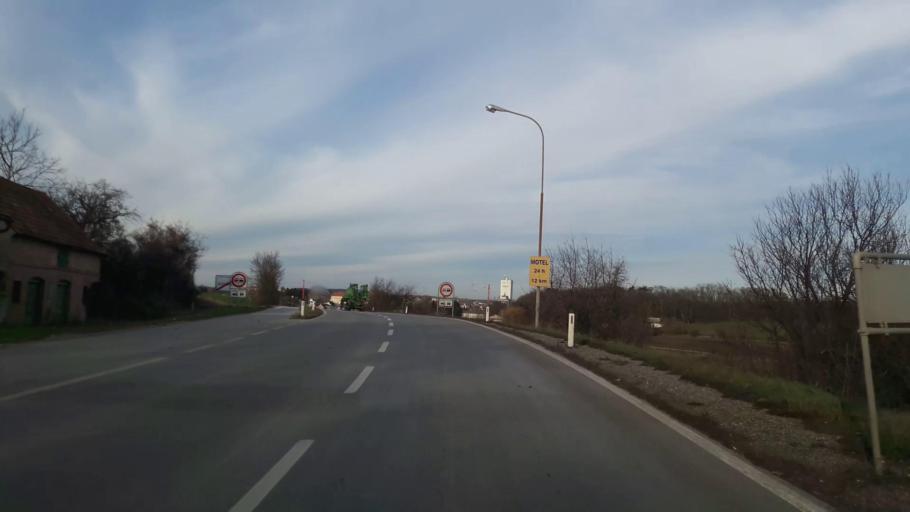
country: AT
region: Lower Austria
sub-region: Politischer Bezirk Mistelbach
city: Gaweinstal
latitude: 48.4661
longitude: 16.5904
